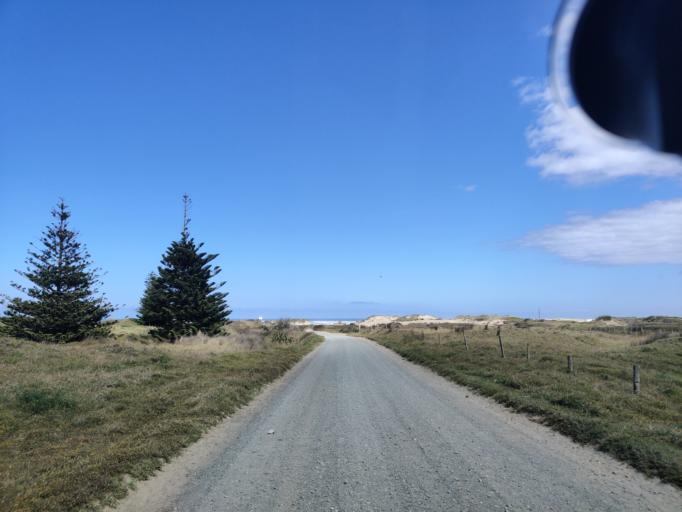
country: NZ
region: Northland
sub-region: Far North District
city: Kaitaia
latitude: -34.8982
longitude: 173.0879
